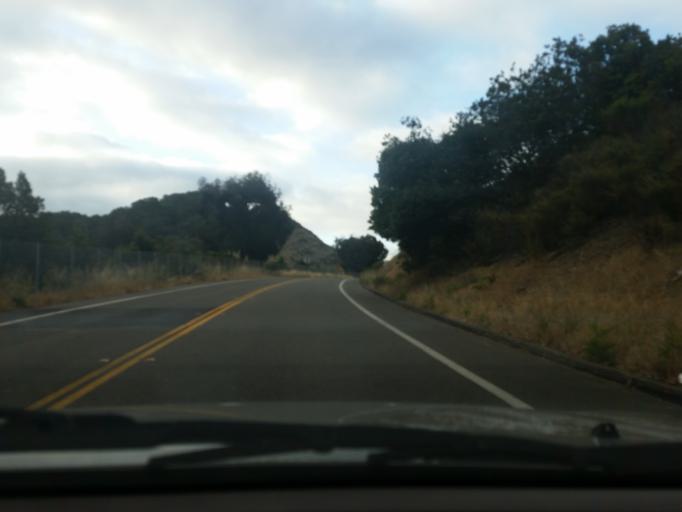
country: US
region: California
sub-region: San Luis Obispo County
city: Avila Beach
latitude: 35.1790
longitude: -120.6997
